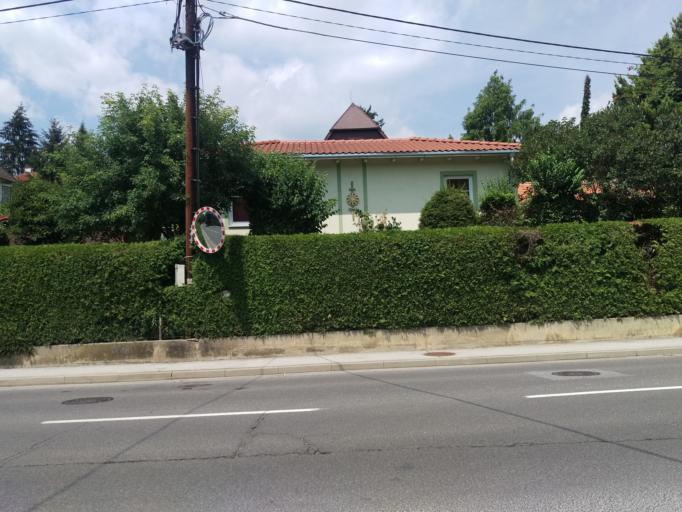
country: AT
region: Styria
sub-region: Graz Stadt
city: Mariatrost
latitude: 47.1003
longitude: 15.4786
